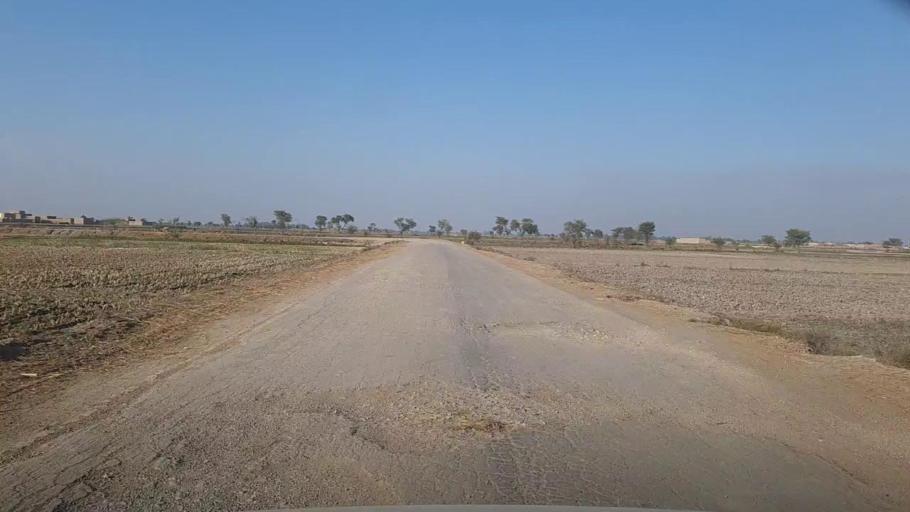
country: PK
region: Sindh
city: Phulji
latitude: 26.8650
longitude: 67.7946
